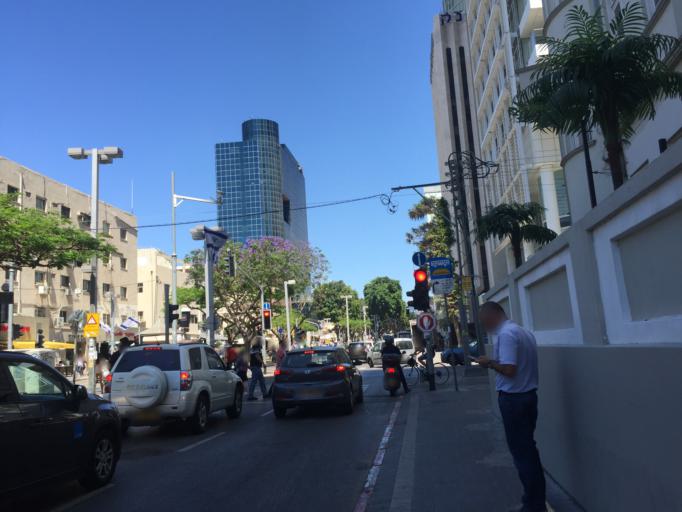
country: IL
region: Tel Aviv
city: Tel Aviv
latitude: 32.0633
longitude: 34.7727
